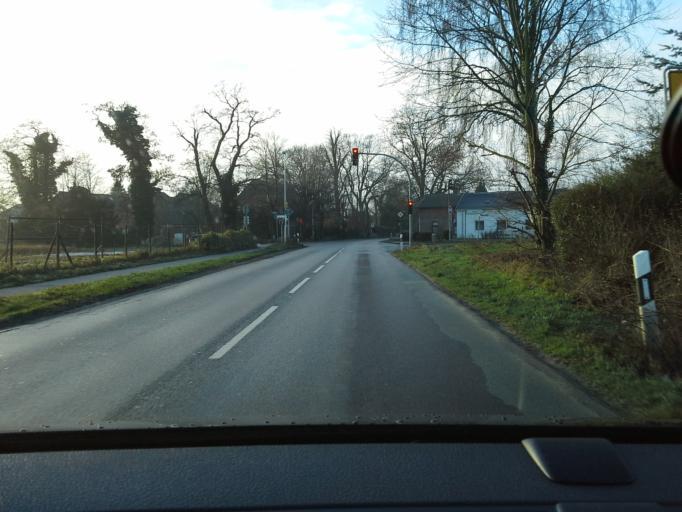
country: DE
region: Schleswig-Holstein
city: Appen
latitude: 53.6391
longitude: 9.7620
